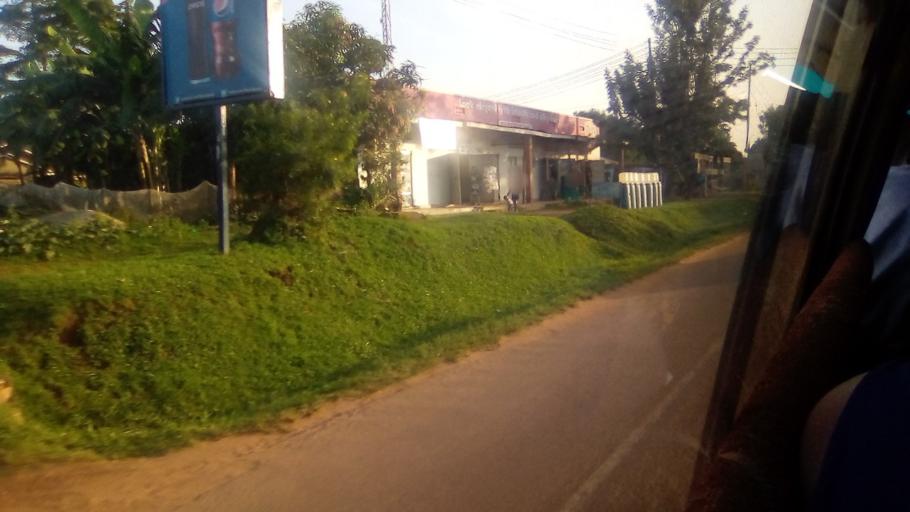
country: UG
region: Central Region
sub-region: Wakiso District
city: Kajansi
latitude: 0.1459
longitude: 32.5450
